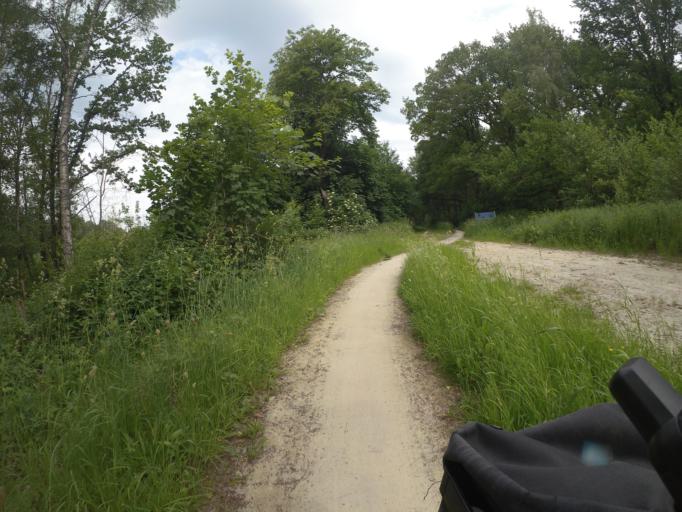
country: NL
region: Drenthe
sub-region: Gemeente Assen
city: Assen
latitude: 52.9930
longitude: 6.4365
